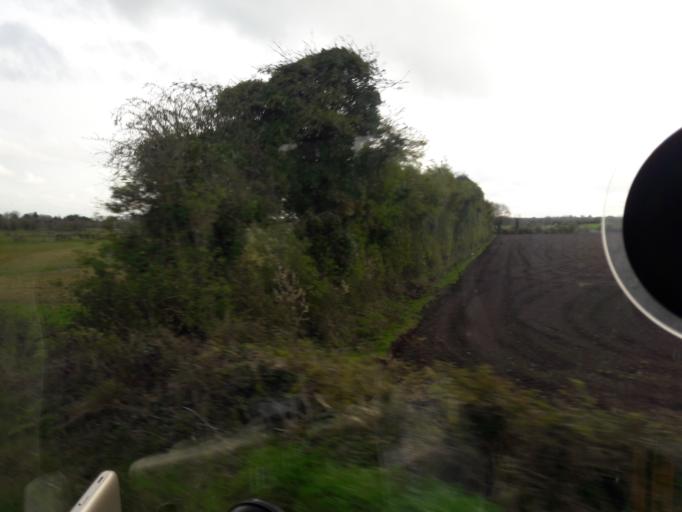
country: IE
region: Leinster
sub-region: An Iarmhi
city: Rathwire
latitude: 53.4909
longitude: -7.1407
